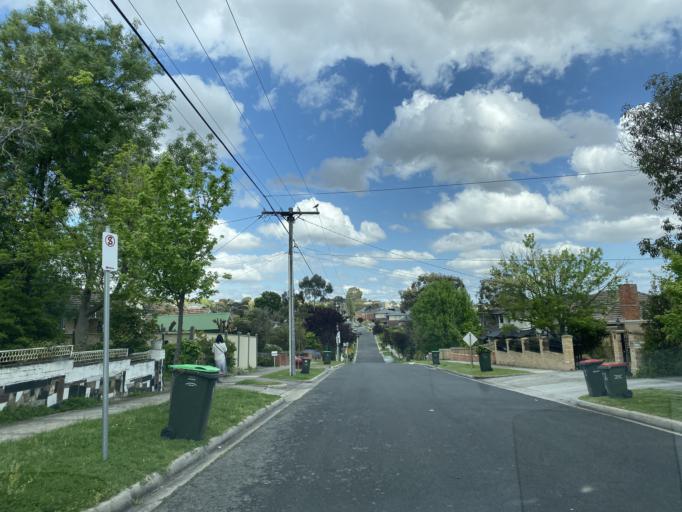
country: AU
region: Victoria
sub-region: Whitehorse
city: Burwood
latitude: -37.8525
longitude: 145.1144
